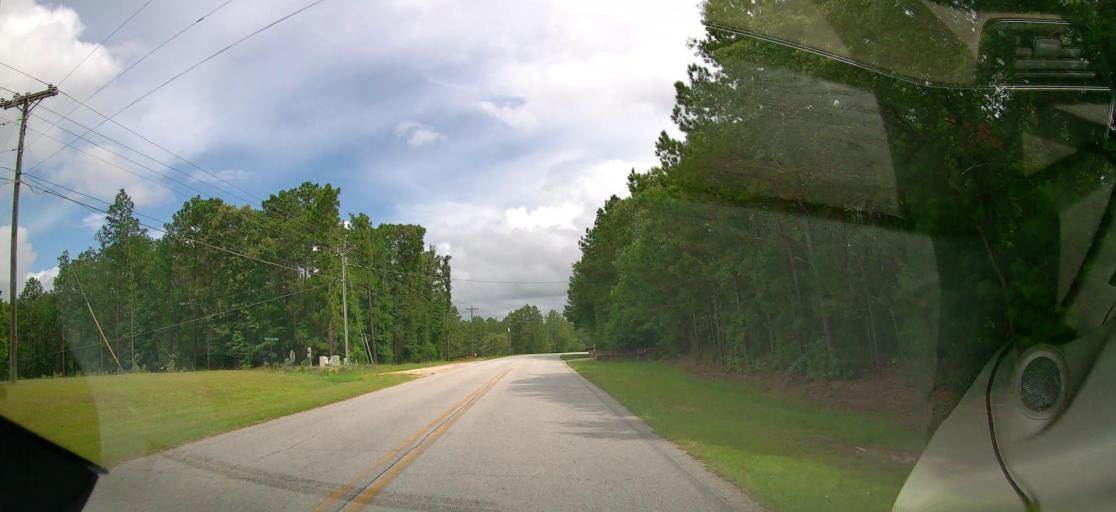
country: US
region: Georgia
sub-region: Peach County
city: Byron
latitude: 32.7052
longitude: -83.7805
